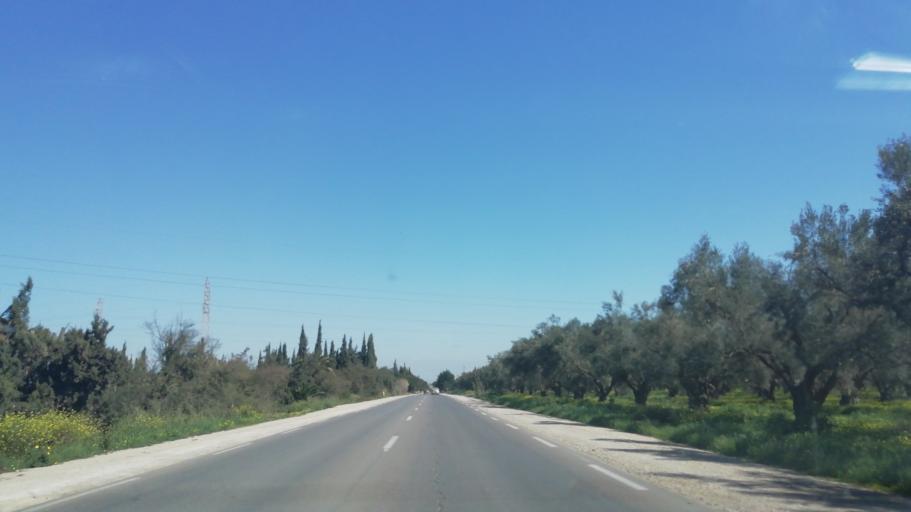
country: DZ
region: Mascara
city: Sig
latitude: 35.5577
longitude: -0.1008
